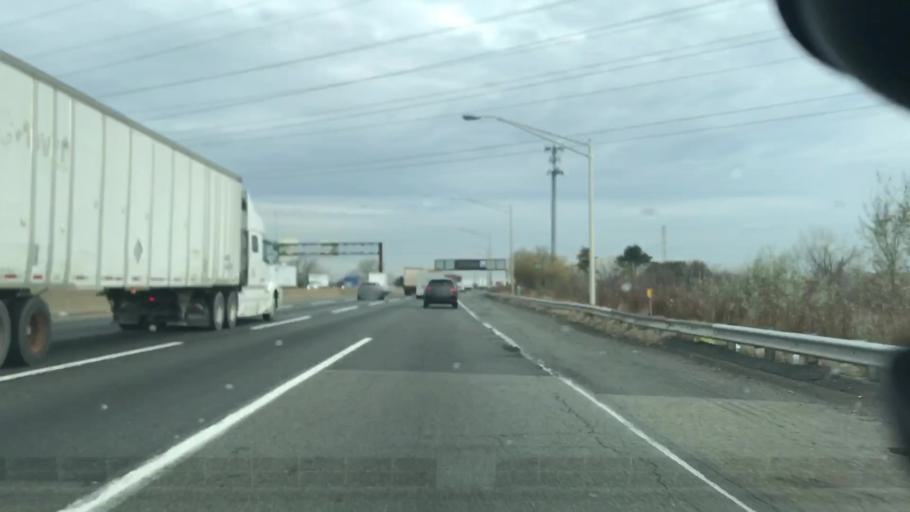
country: US
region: New Jersey
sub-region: Hudson County
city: Kearny
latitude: 40.7572
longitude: -74.1168
